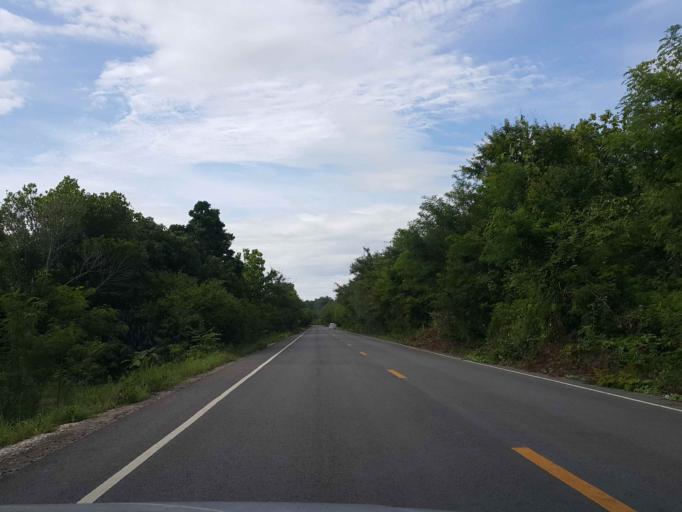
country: TH
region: Sukhothai
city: Thung Saliam
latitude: 17.2873
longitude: 99.5270
